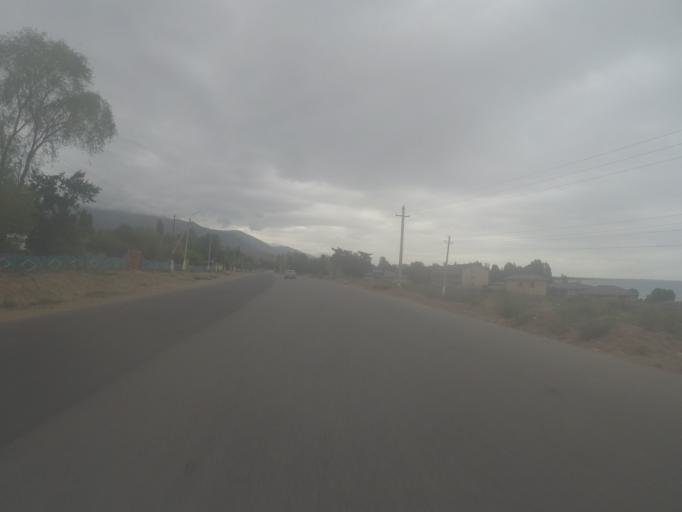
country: KG
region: Ysyk-Koel
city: Cholpon-Ata
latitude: 42.6828
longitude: 77.3356
